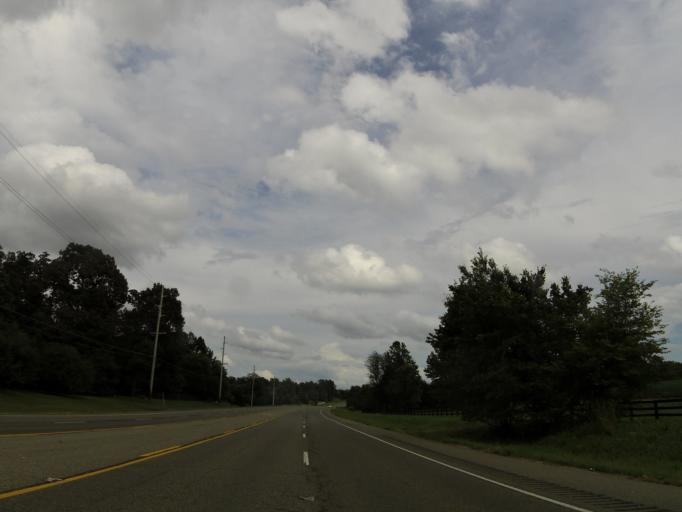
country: US
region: Kentucky
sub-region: McCracken County
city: Massac
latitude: 37.0475
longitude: -88.6897
